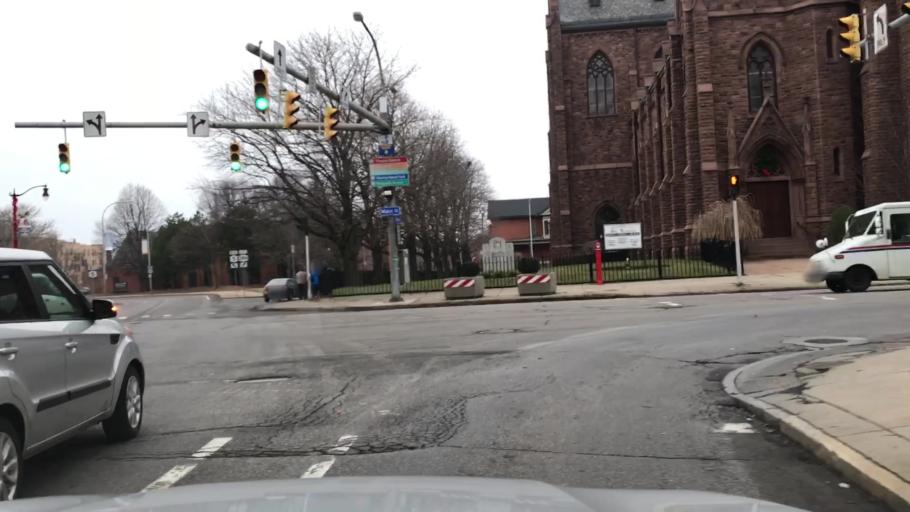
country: US
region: New York
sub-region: Erie County
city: Buffalo
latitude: 42.8953
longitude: -78.8710
